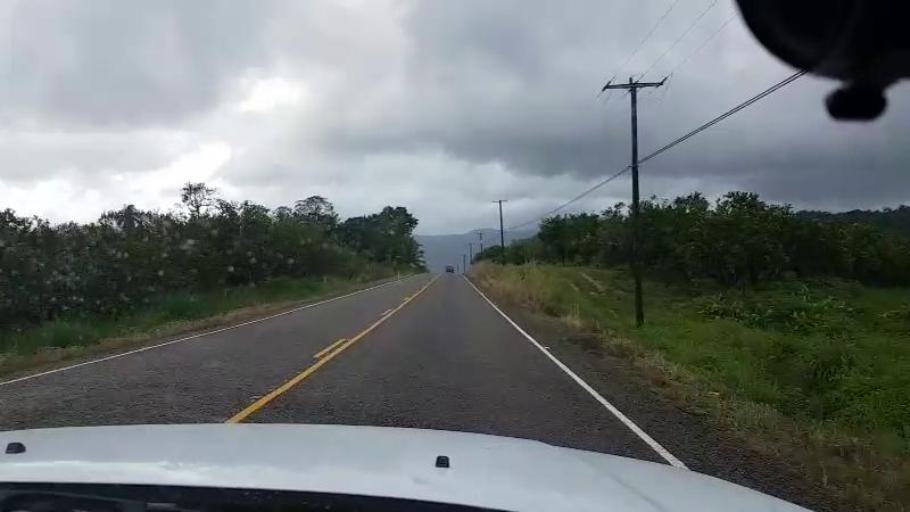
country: BZ
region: Cayo
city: Belmopan
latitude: 17.1185
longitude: -88.6549
